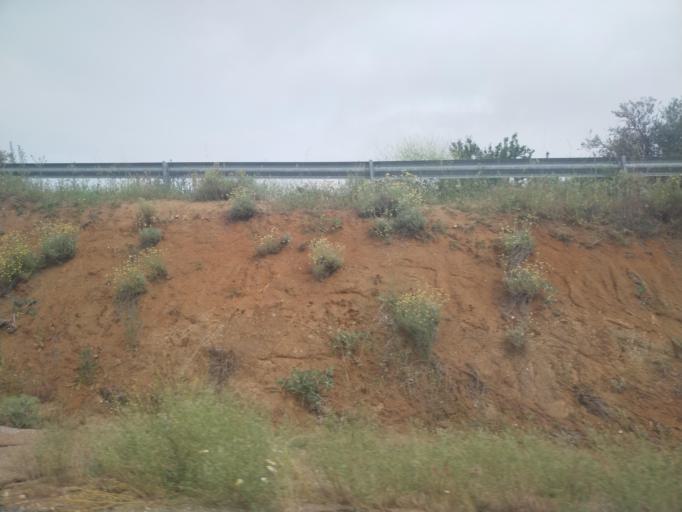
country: ES
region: Castille-La Mancha
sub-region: Province of Toledo
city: Polan
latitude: 39.7856
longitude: -4.1581
